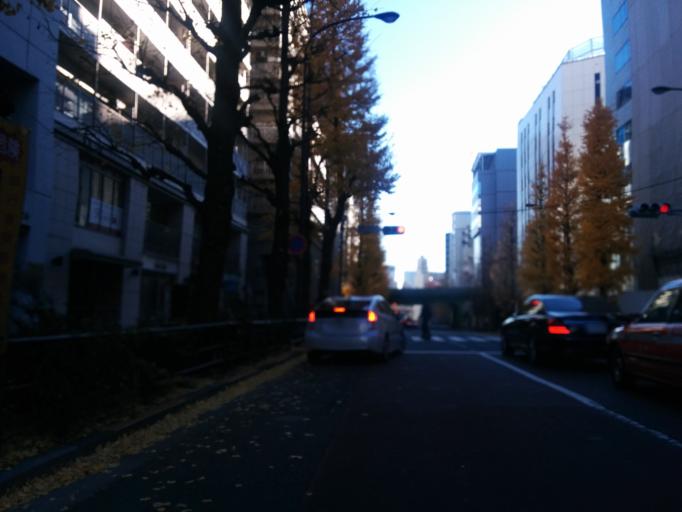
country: JP
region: Tokyo
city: Tokyo
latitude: 35.6827
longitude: 139.7046
